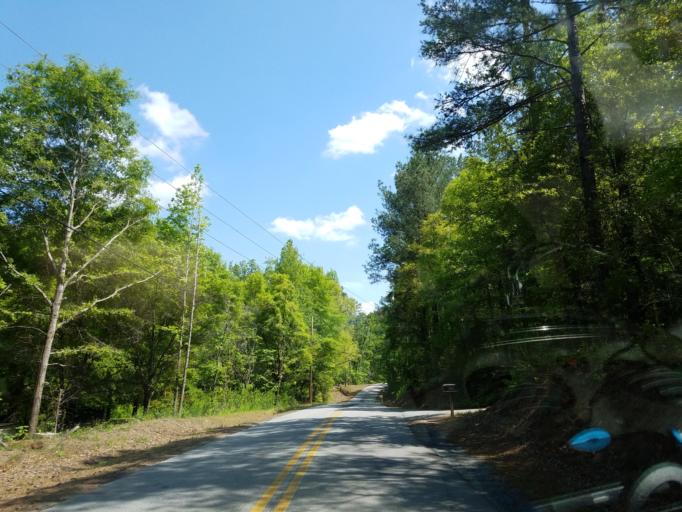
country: US
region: Georgia
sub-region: Monroe County
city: Forsyth
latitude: 33.1235
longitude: -83.9669
